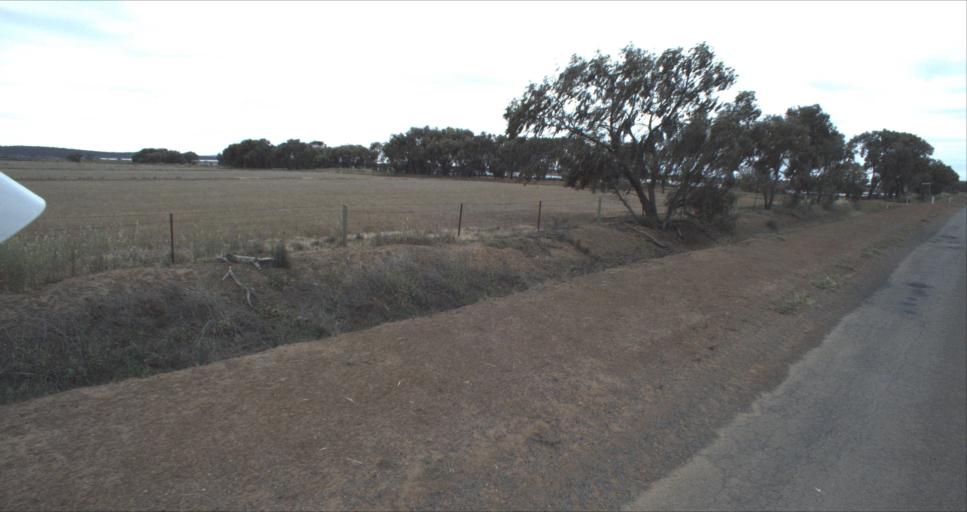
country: AU
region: New South Wales
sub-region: Leeton
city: Leeton
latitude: -34.4116
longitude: 146.3402
